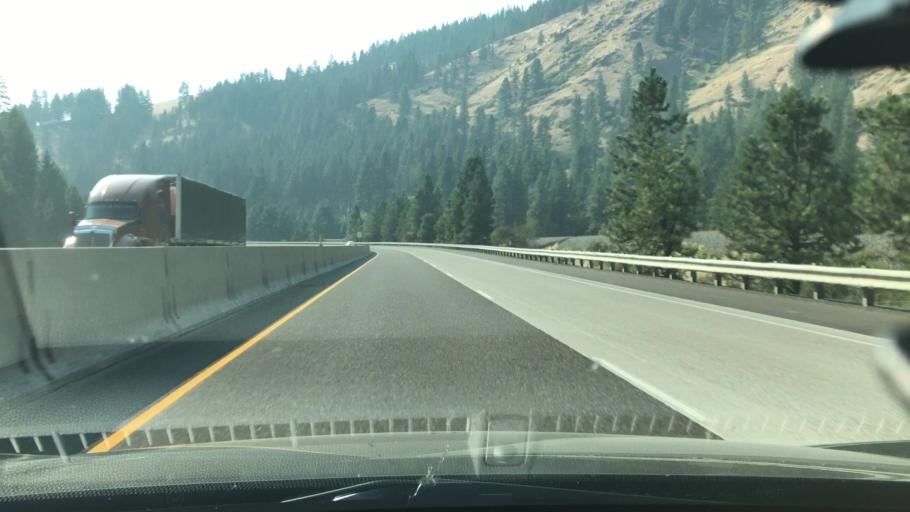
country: US
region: Oregon
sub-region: Union County
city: La Grande
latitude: 45.3538
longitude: -118.1851
